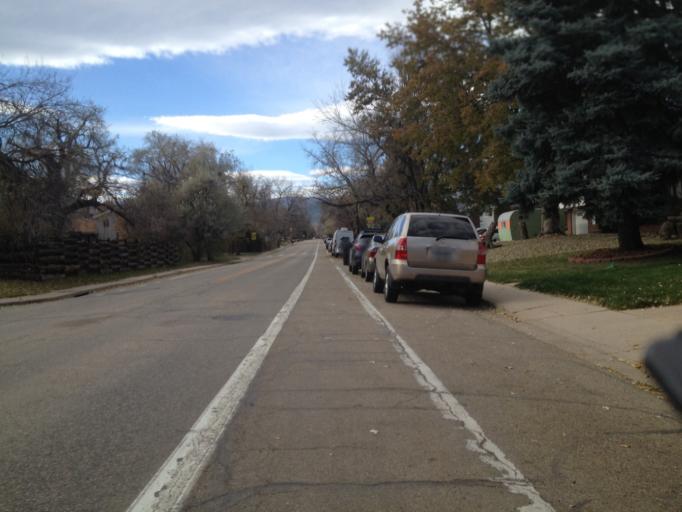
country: US
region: Colorado
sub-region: Boulder County
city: Boulder
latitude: 39.9942
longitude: -105.2497
